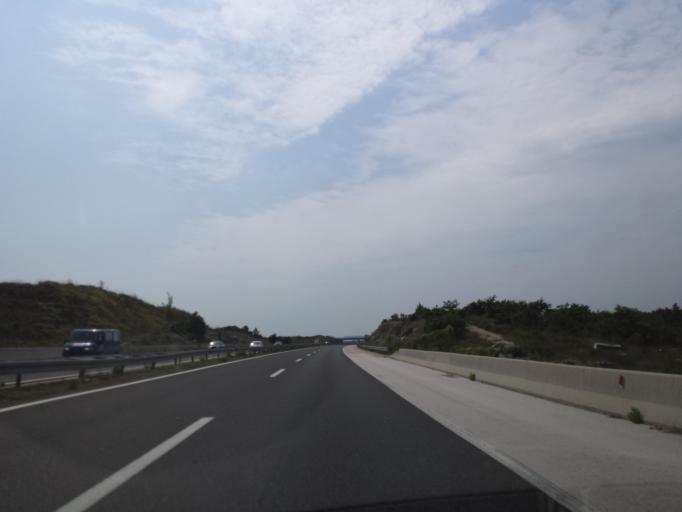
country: HR
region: Zadarska
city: Policnik
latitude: 44.1763
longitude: 15.4276
